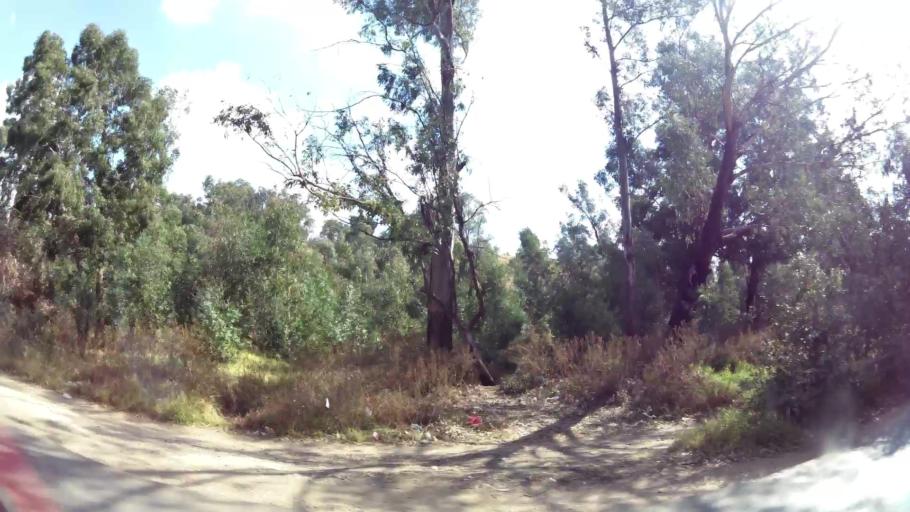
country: ZA
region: Gauteng
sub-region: City of Johannesburg Metropolitan Municipality
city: Roodepoort
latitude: -26.1808
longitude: 27.8700
